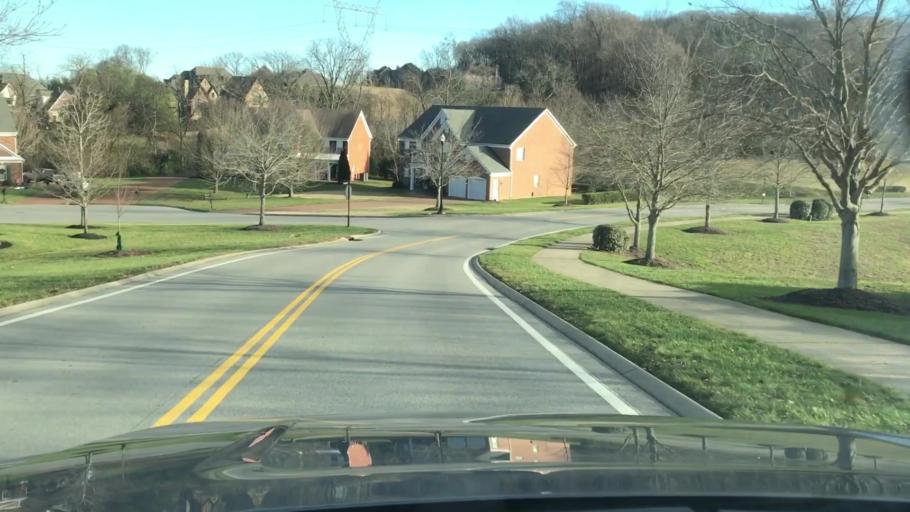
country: US
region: Tennessee
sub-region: Williamson County
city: Brentwood Estates
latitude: 35.9727
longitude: -86.7397
